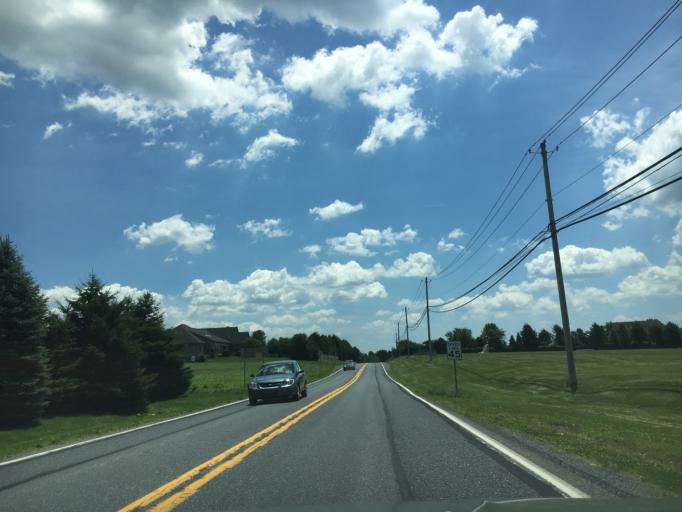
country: US
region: Pennsylvania
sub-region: Lehigh County
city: Schnecksville
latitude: 40.6952
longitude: -75.5924
